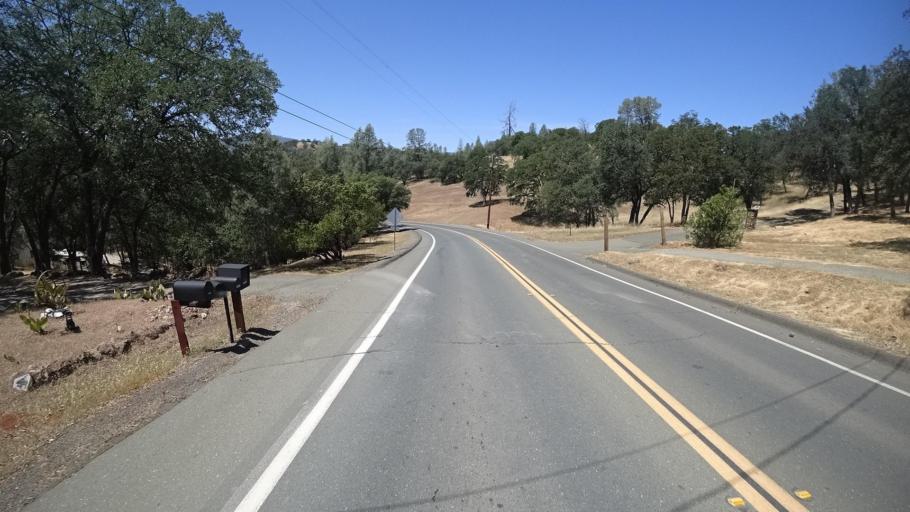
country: US
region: California
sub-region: Lake County
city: Hidden Valley Lake
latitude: 38.8205
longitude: -122.5737
